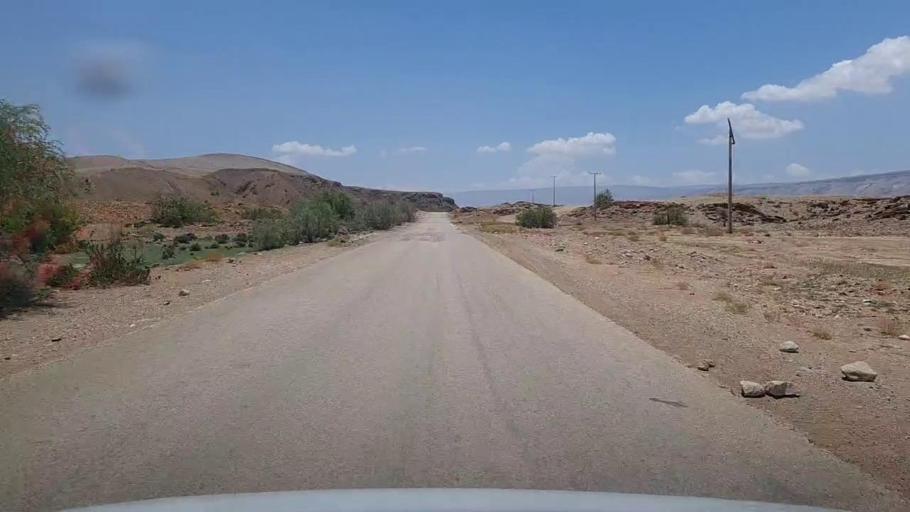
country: PK
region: Sindh
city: Bhan
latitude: 26.3162
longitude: 67.5431
